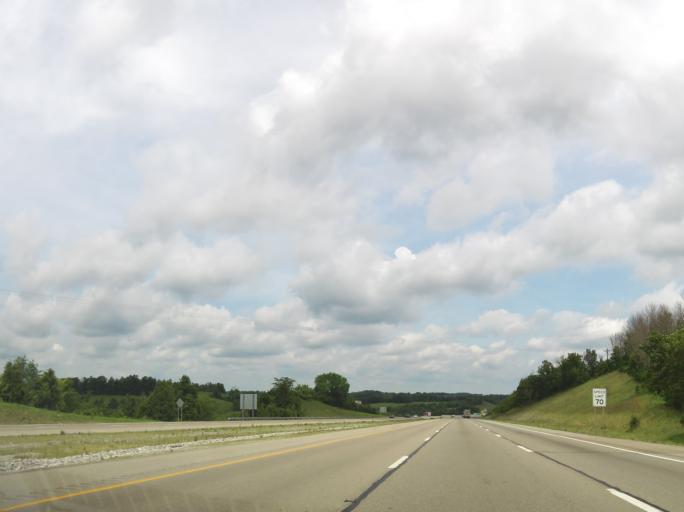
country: US
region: Kentucky
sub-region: Grant County
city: Williamstown
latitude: 38.5001
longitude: -84.5886
